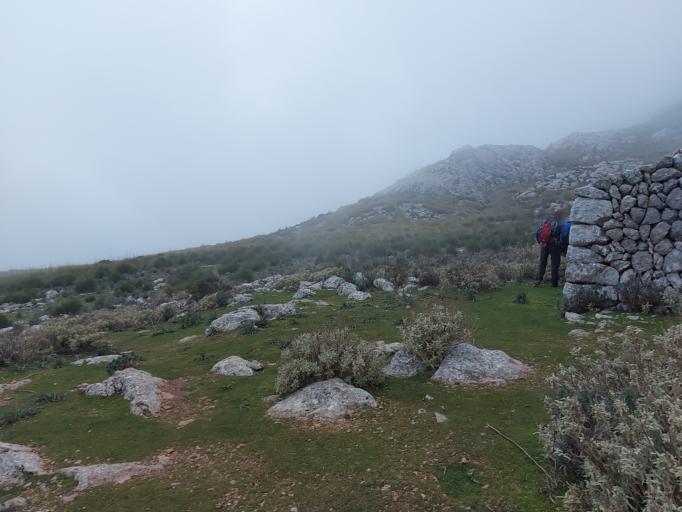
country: ES
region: Balearic Islands
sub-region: Illes Balears
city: Escorca
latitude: 39.8150
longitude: 2.8534
